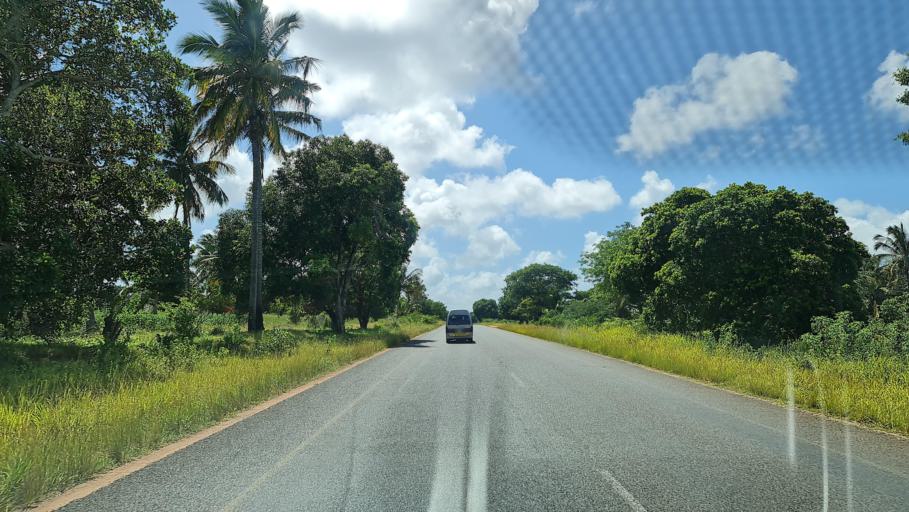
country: MZ
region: Inhambane
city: Maxixe
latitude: -24.5411
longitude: 34.9160
